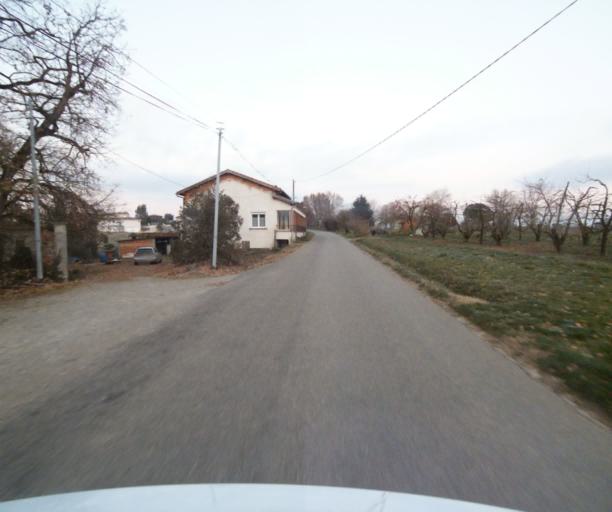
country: FR
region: Midi-Pyrenees
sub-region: Departement du Tarn-et-Garonne
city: Moissac
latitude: 44.1242
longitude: 1.0608
